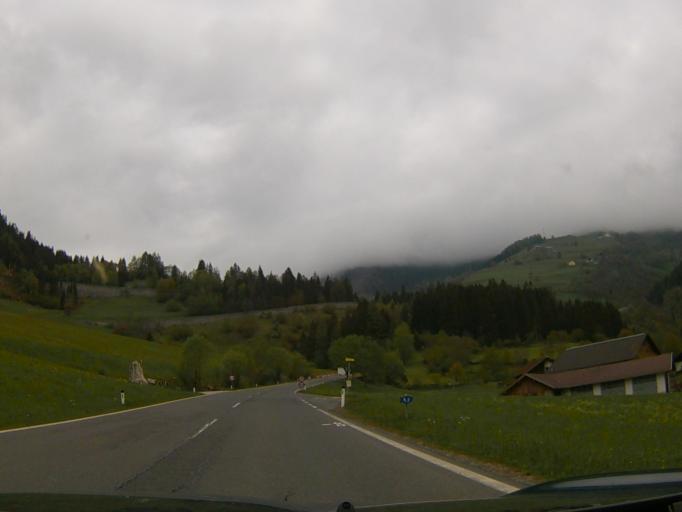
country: AT
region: Carinthia
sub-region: Politischer Bezirk Spittal an der Drau
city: Obervellach
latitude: 46.9629
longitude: 13.1851
